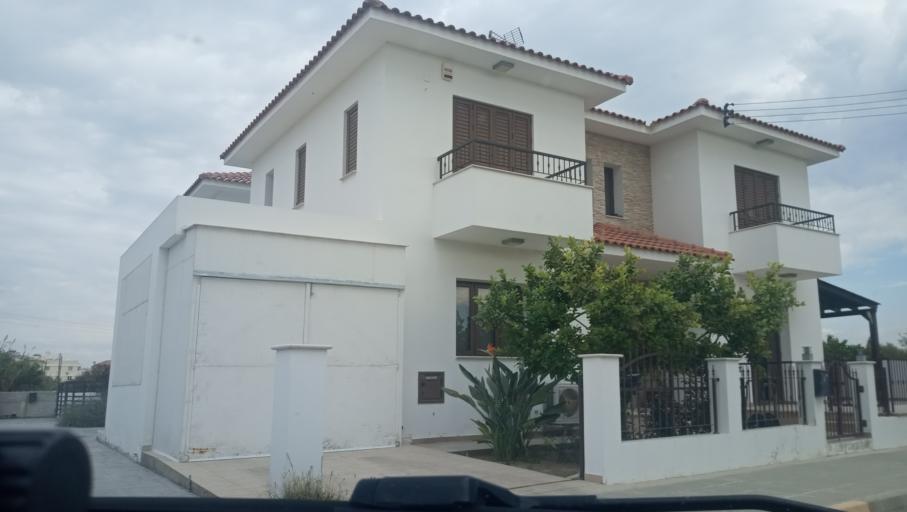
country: CY
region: Larnaka
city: Livadia
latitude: 34.9503
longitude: 33.6314
